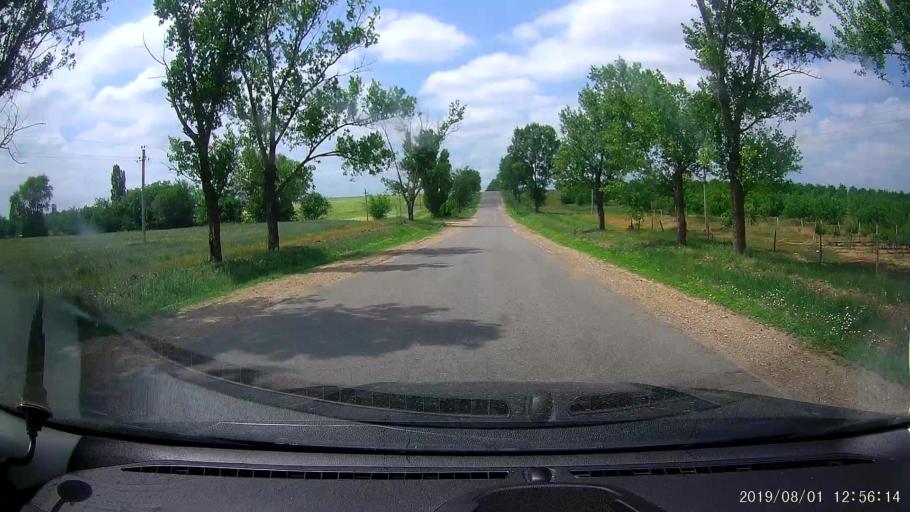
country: MD
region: Gagauzia
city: Vulcanesti
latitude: 45.6923
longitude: 28.4505
